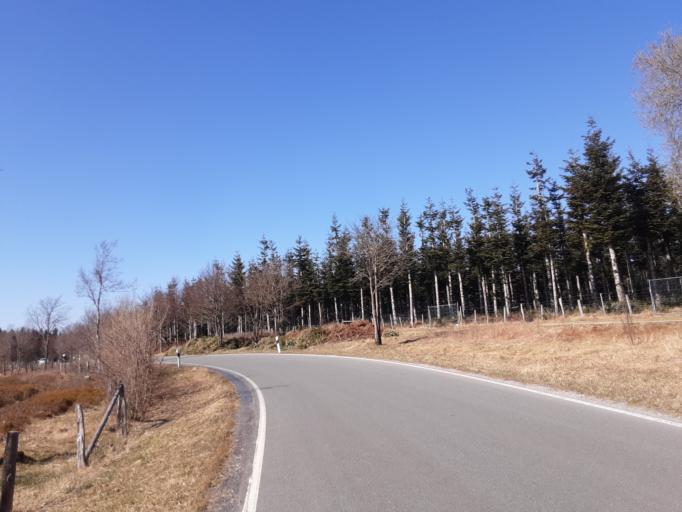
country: DE
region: North Rhine-Westphalia
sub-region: Regierungsbezirk Arnsberg
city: Winterberg
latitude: 51.1966
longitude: 8.4693
